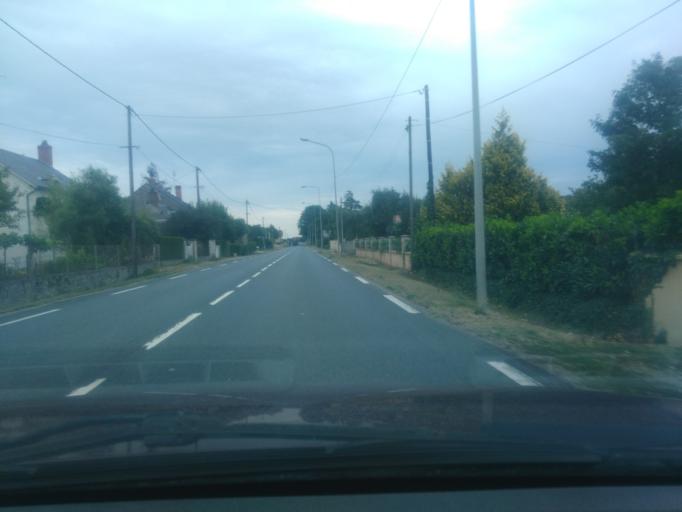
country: FR
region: Centre
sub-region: Departement de l'Indre
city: Belabre
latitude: 46.6310
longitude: 1.2514
